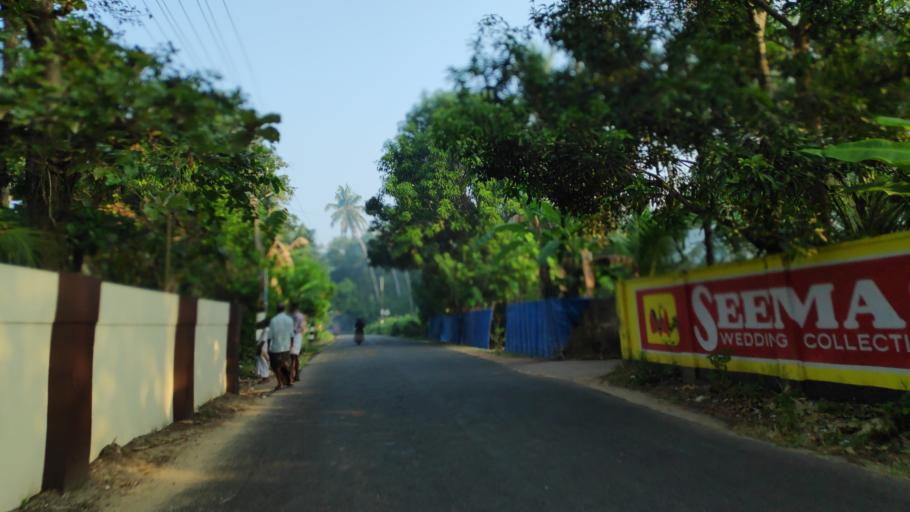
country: IN
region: Kerala
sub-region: Alappuzha
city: Vayalar
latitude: 9.6958
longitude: 76.2902
